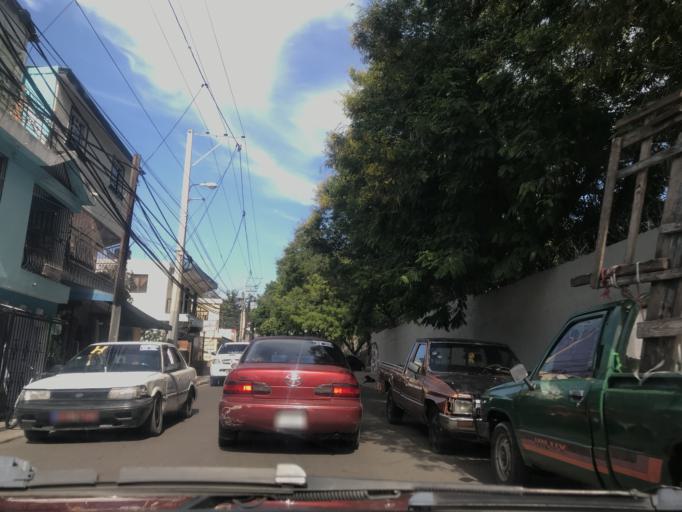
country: DO
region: Santiago
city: Santiago de los Caballeros
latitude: 19.4278
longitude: -70.6837
